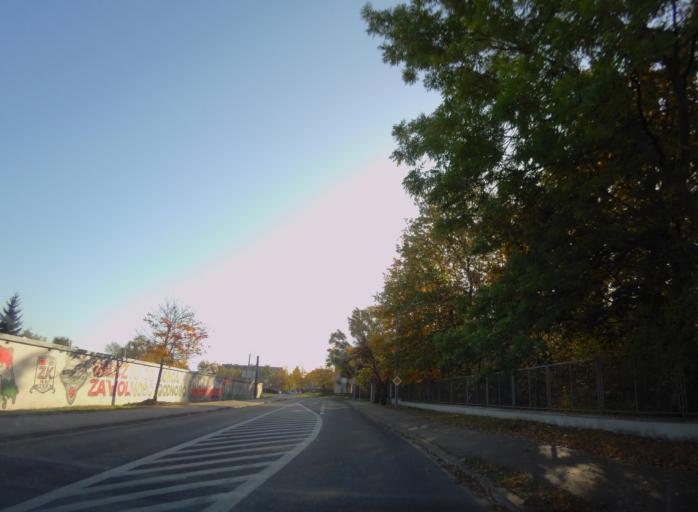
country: PL
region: Masovian Voivodeship
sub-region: Powiat pruszkowski
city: Granica
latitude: 52.1523
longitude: 20.7877
